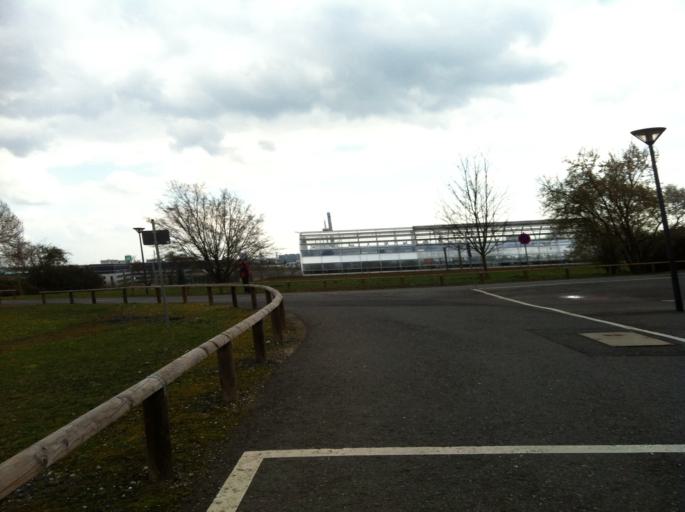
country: DE
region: Hesse
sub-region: Regierungsbezirk Darmstadt
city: Steinbach am Taunus
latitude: 50.1713
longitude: 8.6290
